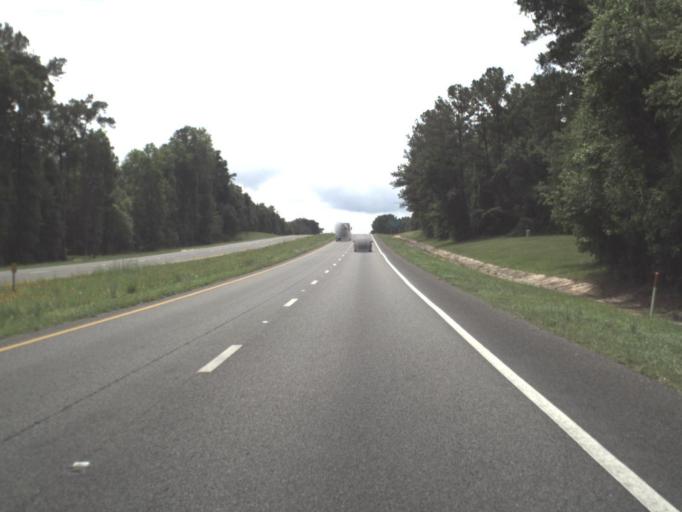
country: US
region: Florida
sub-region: Nassau County
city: Hilliard
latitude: 30.7593
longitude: -81.9655
